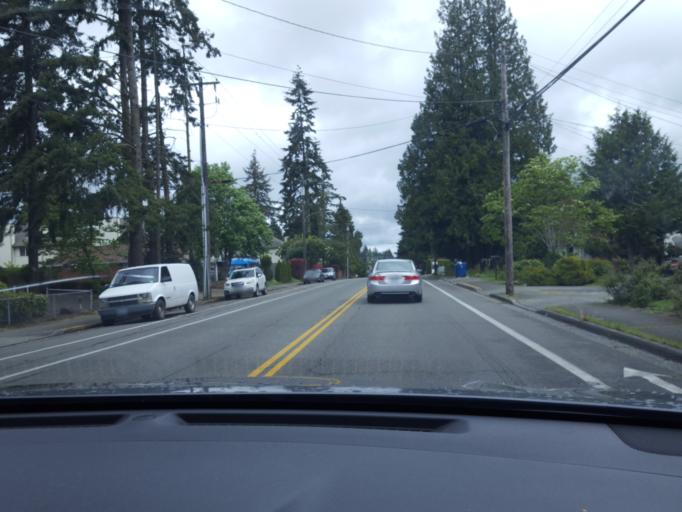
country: US
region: Washington
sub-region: Snohomish County
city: Esperance
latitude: 47.7893
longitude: -122.3355
